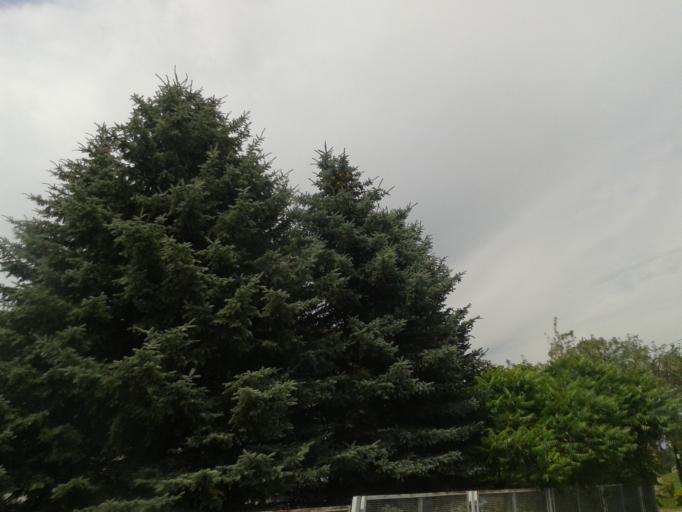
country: DE
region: Saxony
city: Reinsberg
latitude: 51.0002
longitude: 13.3353
